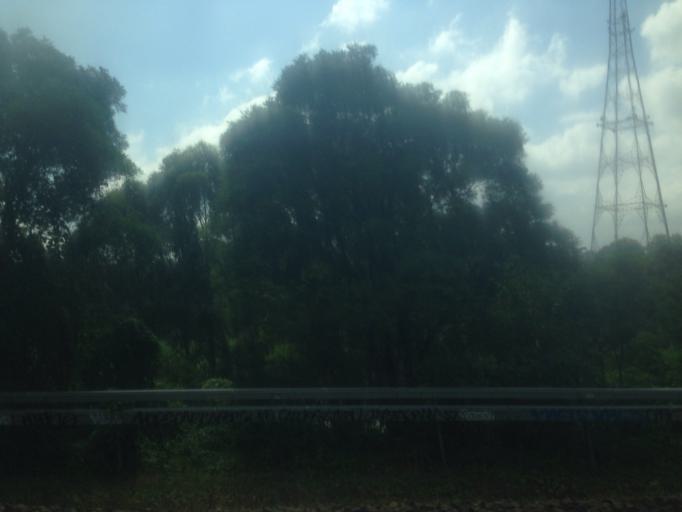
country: AU
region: New South Wales
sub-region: Willoughby
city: Artarmon
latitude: -33.8124
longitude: 151.1918
